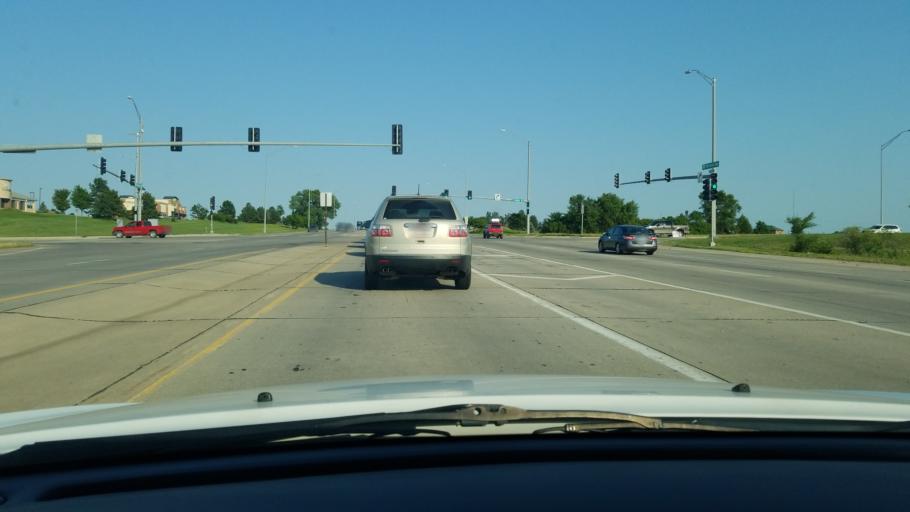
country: US
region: Nebraska
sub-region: Lancaster County
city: Lincoln
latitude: 40.7362
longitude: -96.6070
